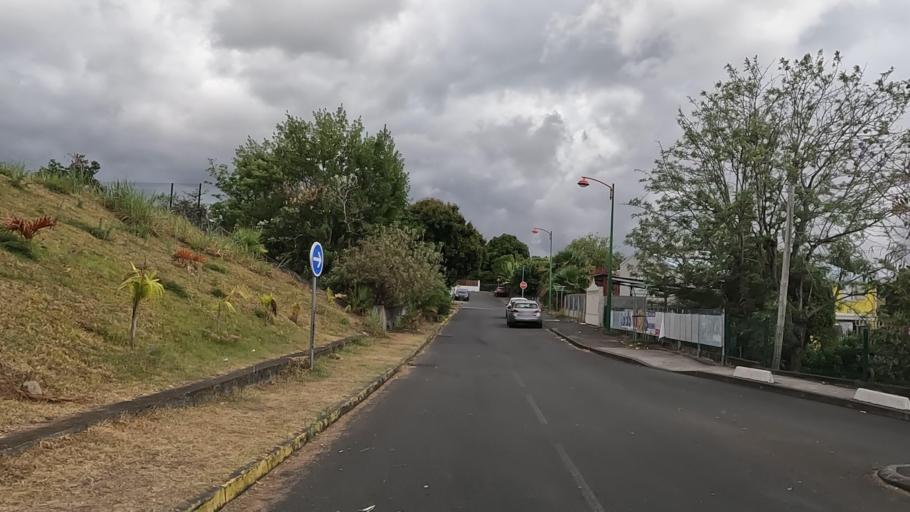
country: RE
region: Reunion
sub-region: Reunion
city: Le Tampon
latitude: -21.2787
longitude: 55.5053
